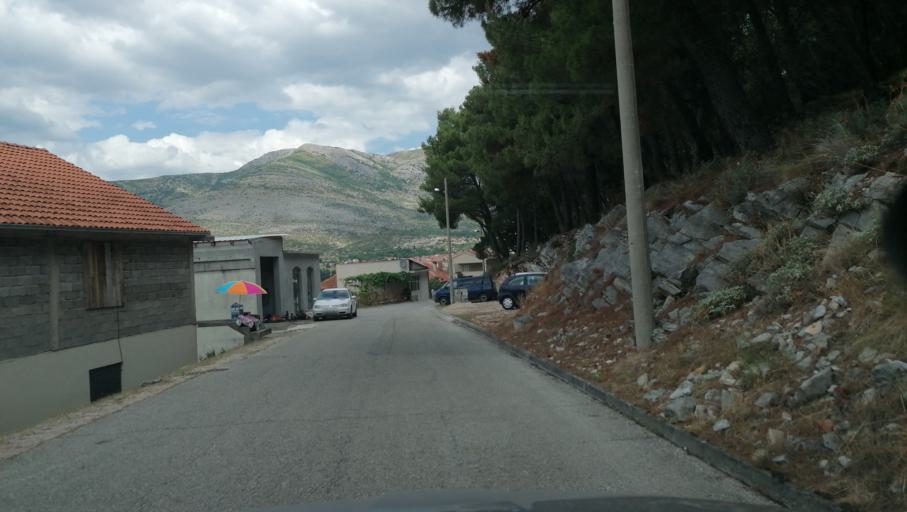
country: BA
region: Republika Srpska
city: Trebinje
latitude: 42.7103
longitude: 18.3574
